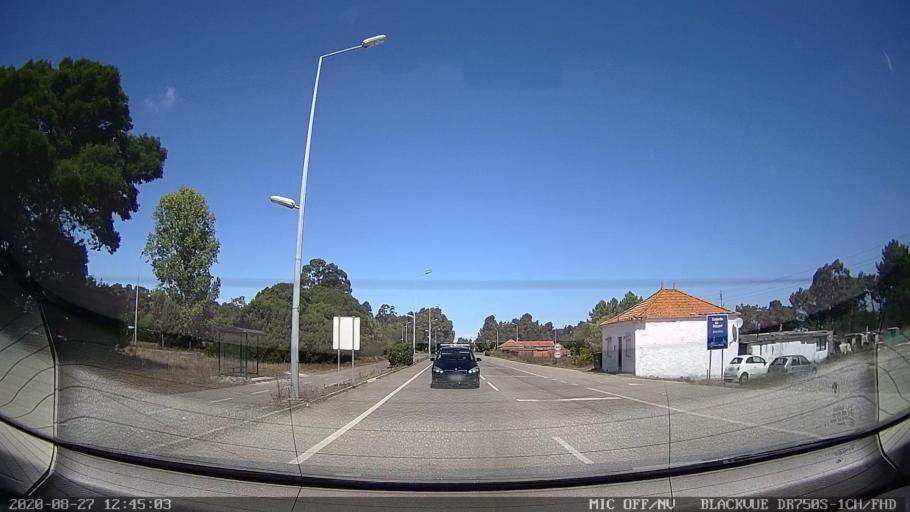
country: PT
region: Aveiro
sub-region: Ilhavo
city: Ilhavo
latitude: 40.6215
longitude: -8.6857
